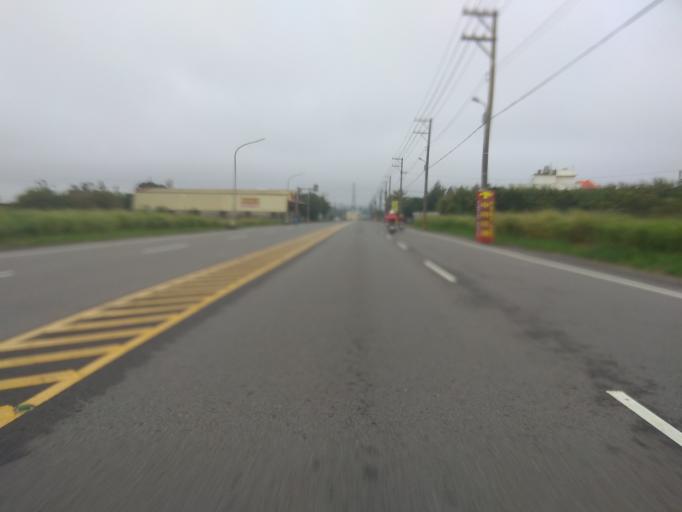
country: TW
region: Taiwan
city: Taoyuan City
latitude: 25.0163
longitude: 121.1288
